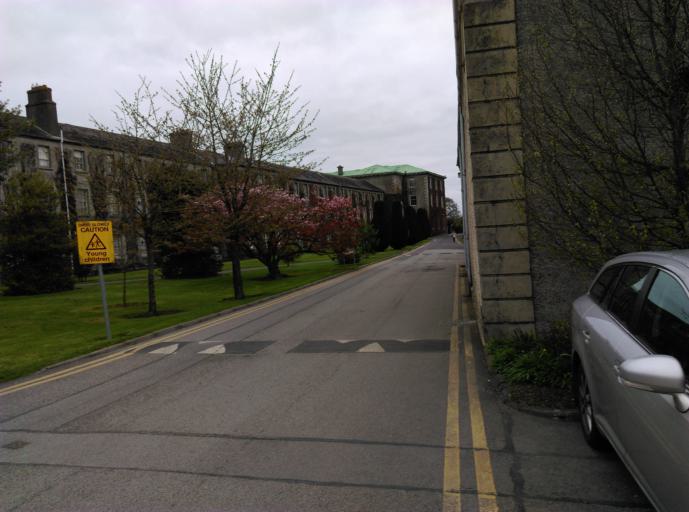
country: IE
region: Leinster
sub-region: Kildare
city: Maynooth
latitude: 53.3789
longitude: -6.5968
